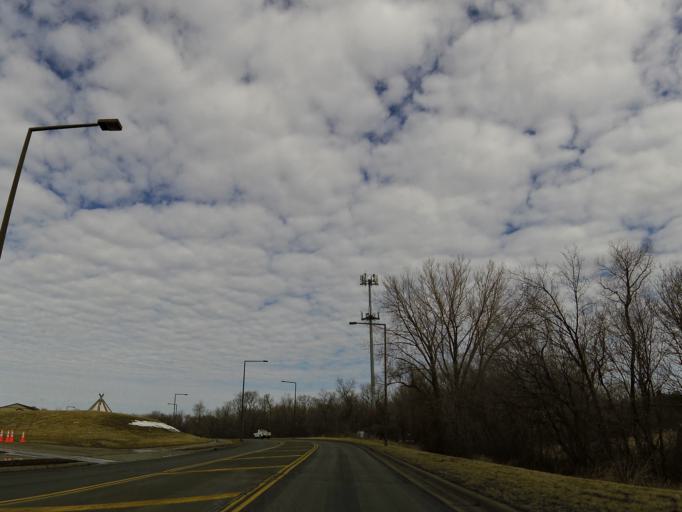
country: US
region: Minnesota
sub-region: Scott County
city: Prior Lake
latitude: 44.7337
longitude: -93.4712
